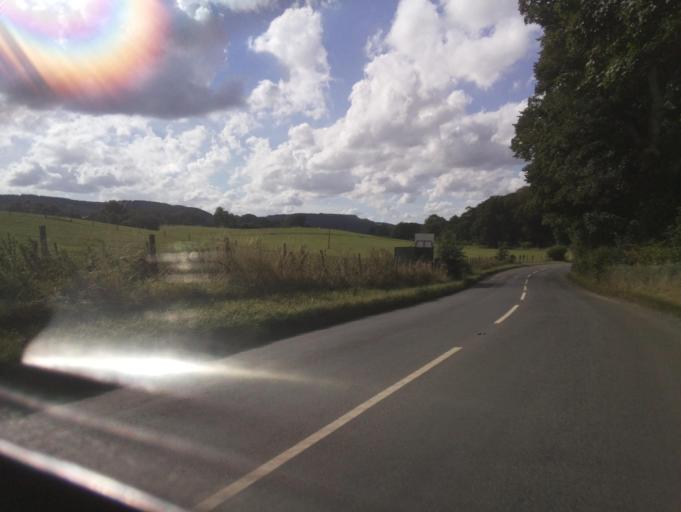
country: GB
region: England
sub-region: North Yorkshire
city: Leyburn
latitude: 54.2624
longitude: -1.7271
